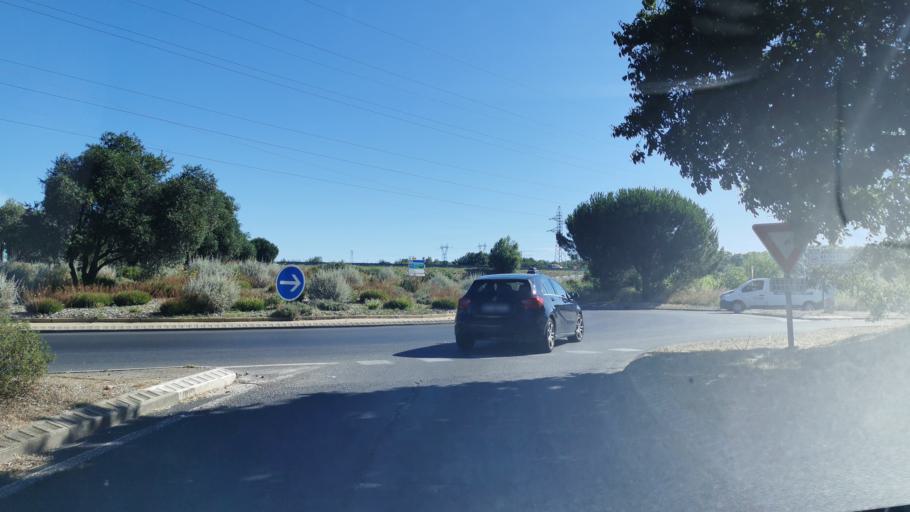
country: FR
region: Languedoc-Roussillon
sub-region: Departement de l'Herault
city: Beziers
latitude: 43.3658
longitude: 3.2104
